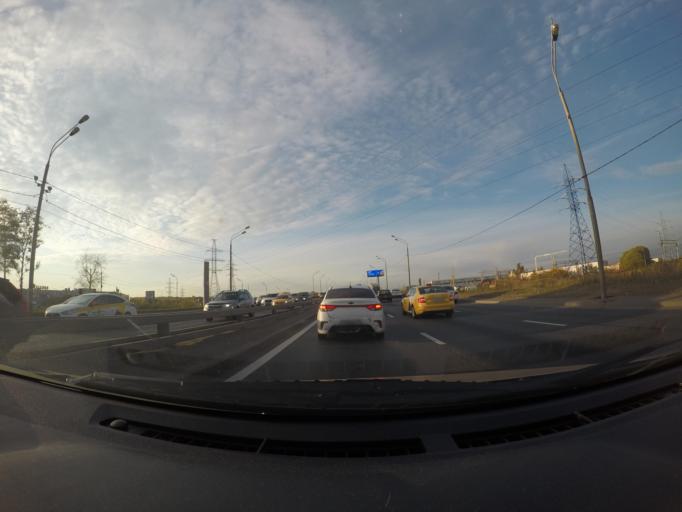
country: RU
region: Moscow
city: Khimki
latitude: 55.9136
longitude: 37.4026
